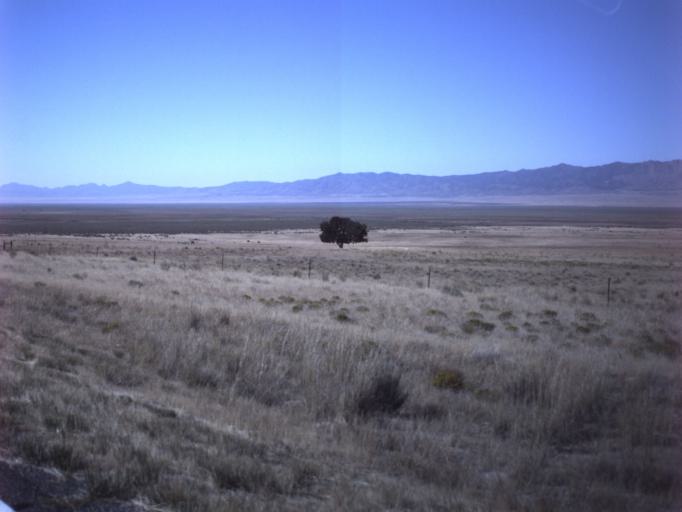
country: US
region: Utah
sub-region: Tooele County
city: Grantsville
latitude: 40.5800
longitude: -112.7259
